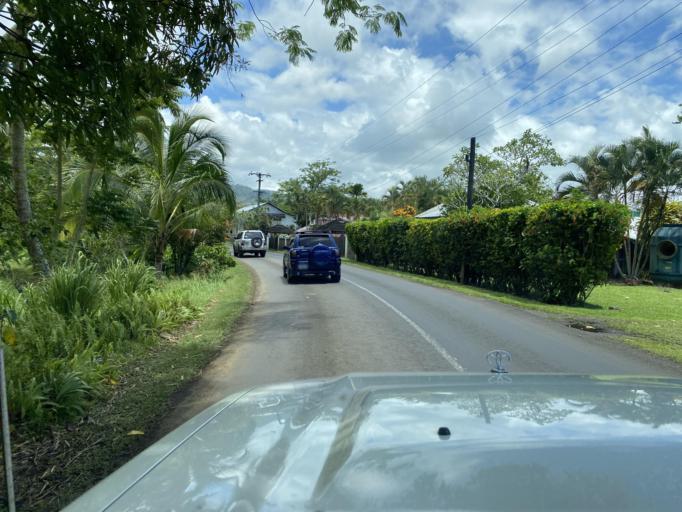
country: WS
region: Tuamasaga
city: Apia
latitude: -13.8505
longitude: -171.7801
